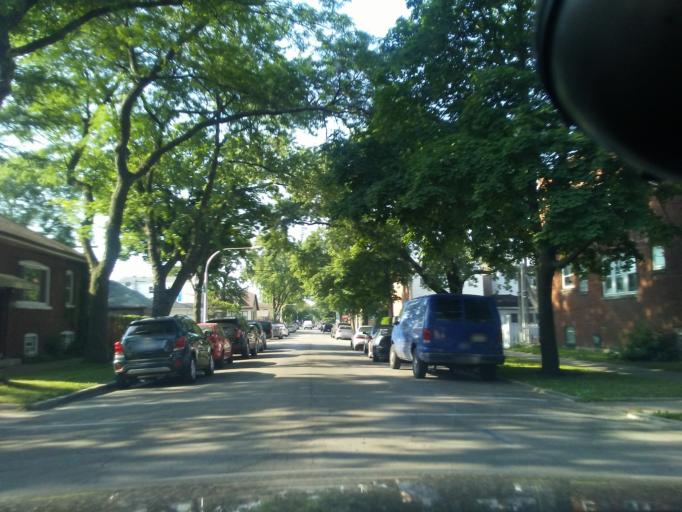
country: US
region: Illinois
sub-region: Cook County
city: Oak Park
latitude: 41.9261
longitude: -87.7513
